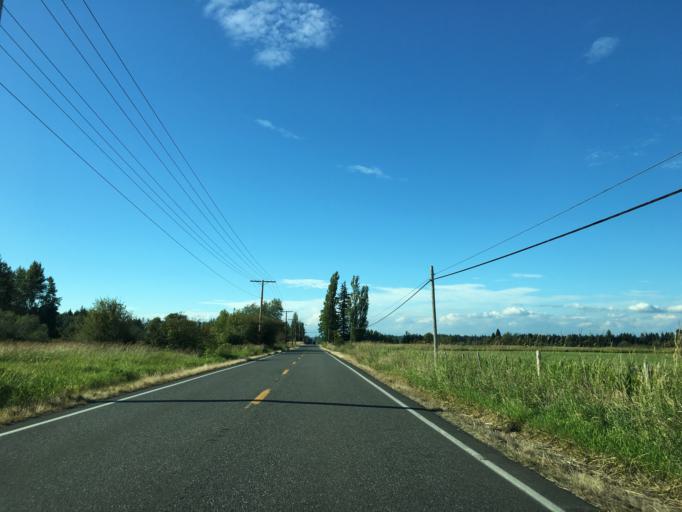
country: US
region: Washington
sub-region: Whatcom County
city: Birch Bay
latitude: 48.9154
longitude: -122.7265
